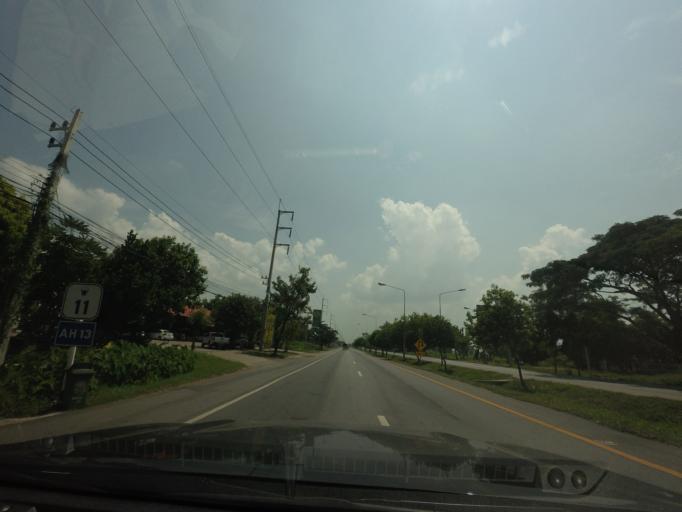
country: TH
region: Uttaradit
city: Uttaradit
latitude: 17.5860
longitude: 100.1381
